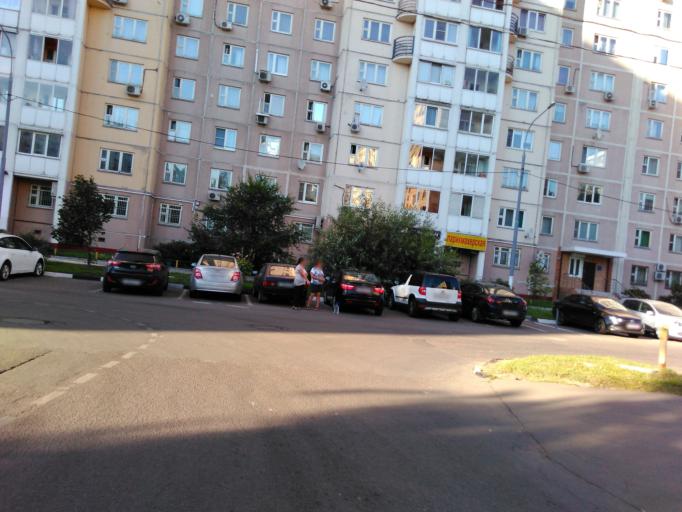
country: RU
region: Moscow
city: Tyoply Stan
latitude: 55.6398
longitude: 37.5130
